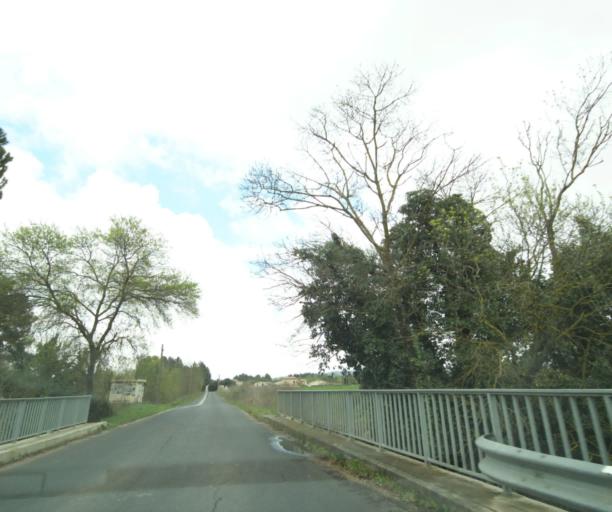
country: FR
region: Languedoc-Roussillon
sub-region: Departement de l'Herault
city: Fabregues
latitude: 43.5547
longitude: 3.7559
